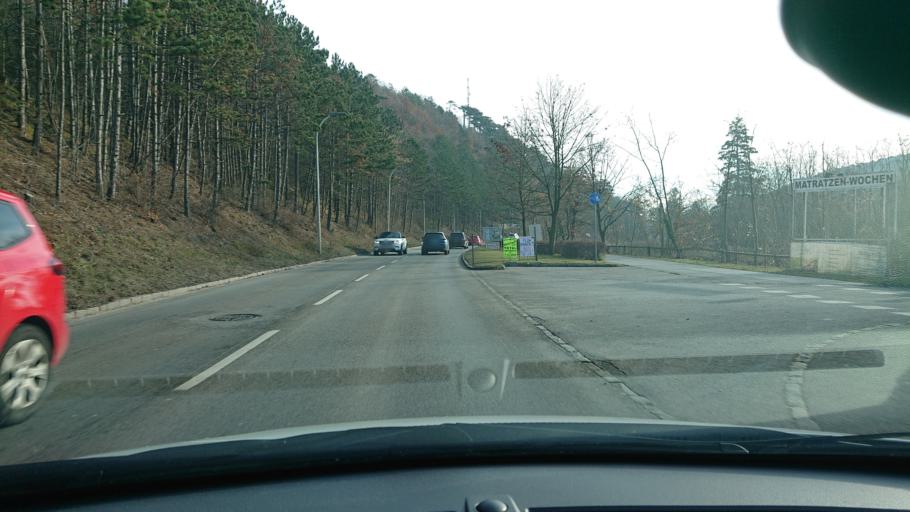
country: AT
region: Lower Austria
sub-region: Politischer Bezirk Baden
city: Hirtenberg
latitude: 47.9334
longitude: 16.1693
